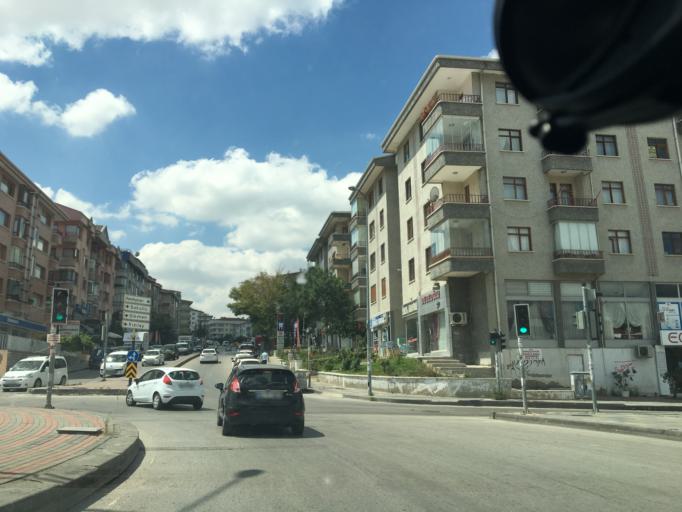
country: TR
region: Ankara
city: Ankara
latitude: 39.8849
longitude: 32.8285
